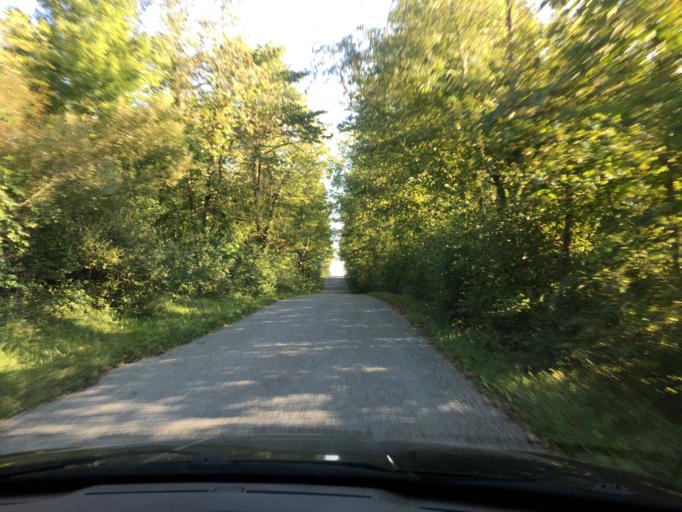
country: US
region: Ohio
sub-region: Logan County
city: West Liberty
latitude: 40.2552
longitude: -83.6627
